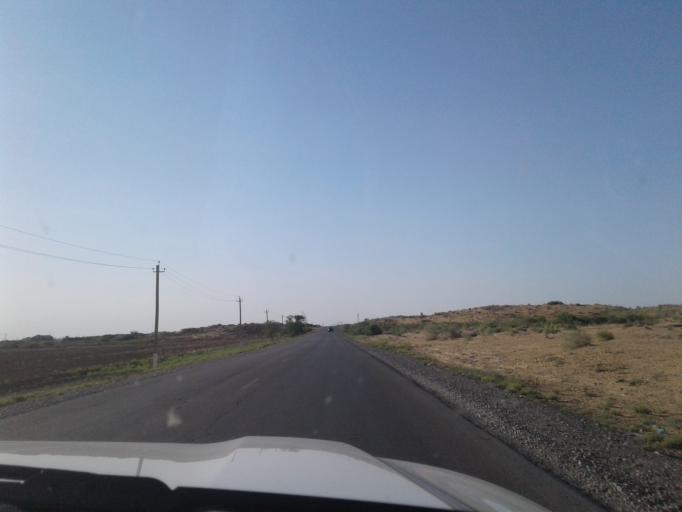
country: TM
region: Mary
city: Yoloeten
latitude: 37.2278
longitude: 62.3741
